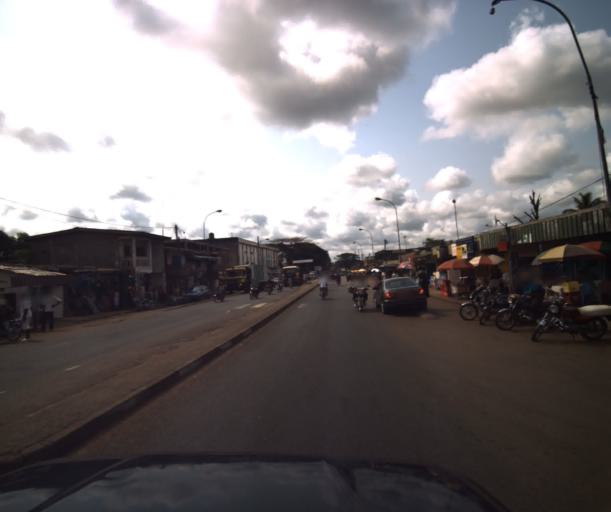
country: CM
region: Littoral
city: Edea
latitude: 3.7977
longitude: 10.1303
